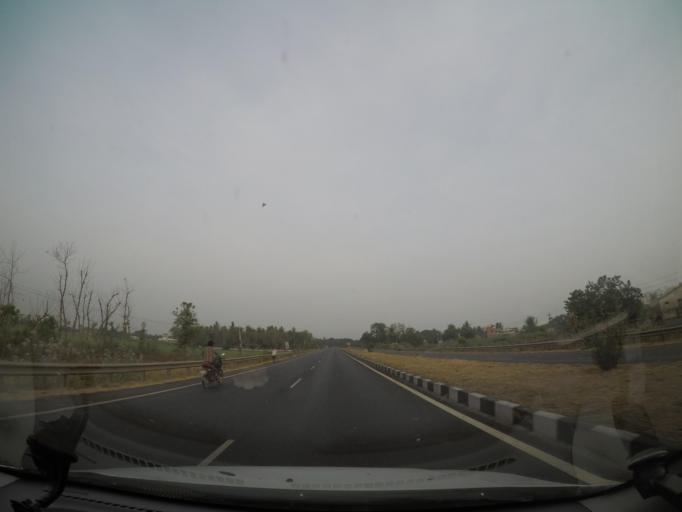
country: IN
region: Andhra Pradesh
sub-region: Krishna
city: Gannavaram
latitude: 16.6100
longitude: 80.9162
